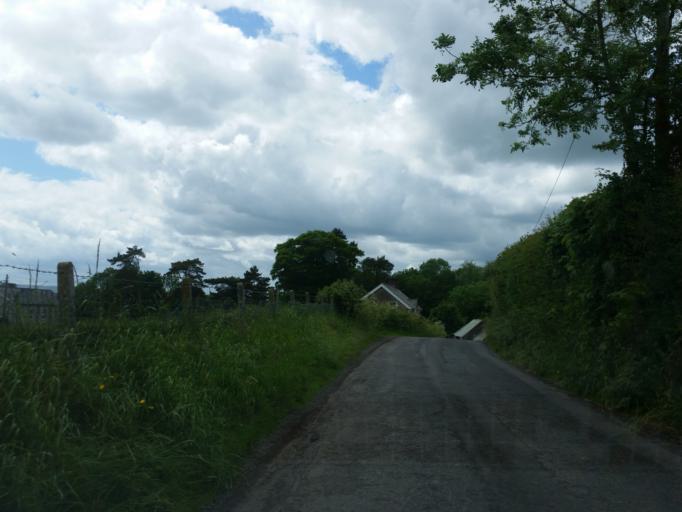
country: IE
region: Ulster
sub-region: County Monaghan
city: Monaghan
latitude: 54.4592
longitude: -7.0760
